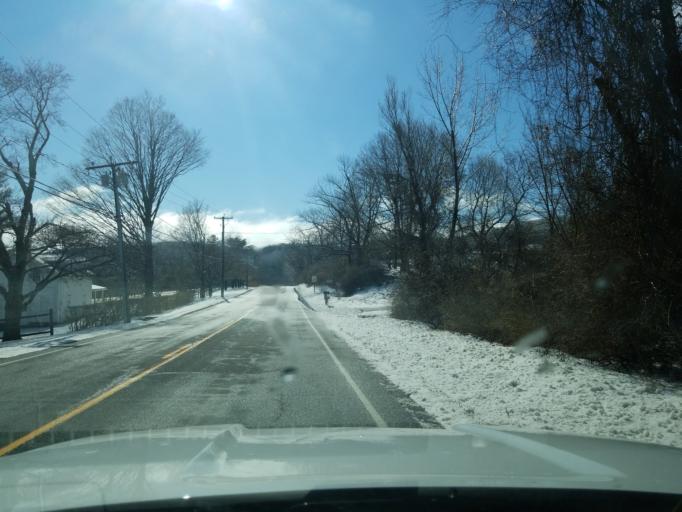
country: US
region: Connecticut
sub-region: Litchfield County
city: Canaan
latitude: 41.9310
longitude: -73.4215
